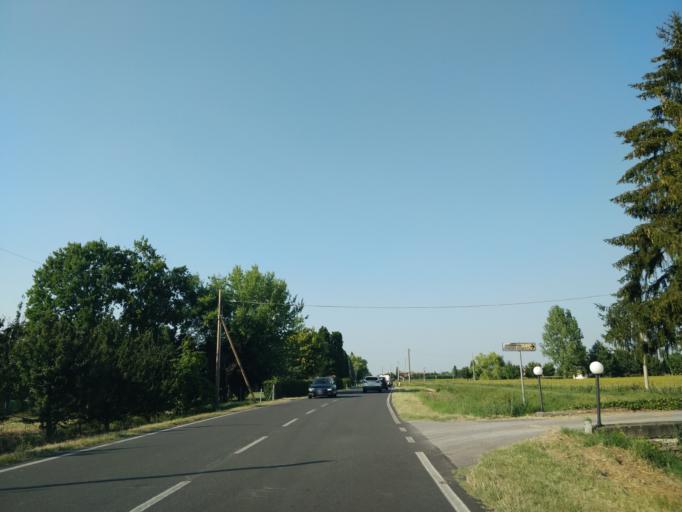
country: IT
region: Emilia-Romagna
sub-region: Provincia di Bologna
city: Argelato
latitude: 44.6276
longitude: 11.3397
